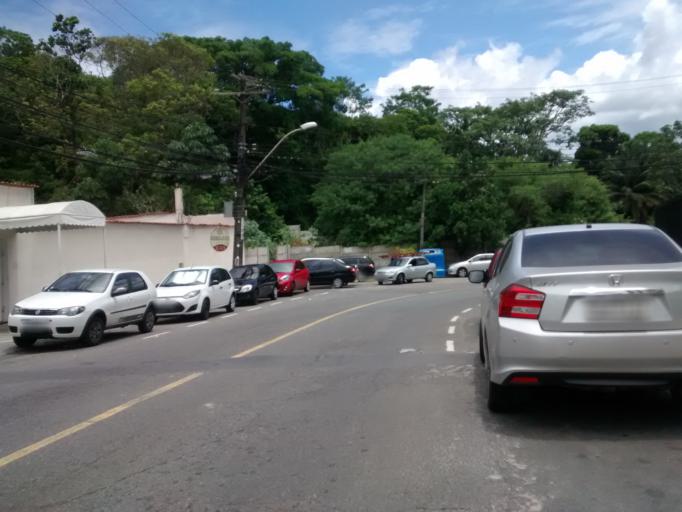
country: BR
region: Bahia
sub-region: Salvador
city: Salvador
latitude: -12.9753
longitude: -38.4414
